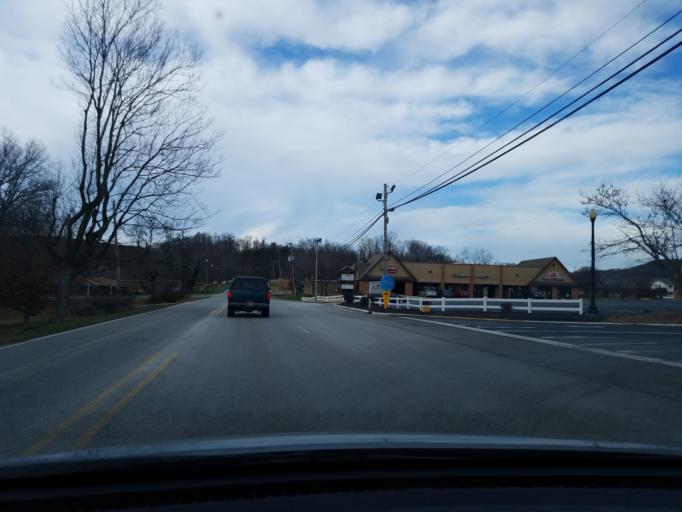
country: US
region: Indiana
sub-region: Floyd County
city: New Albany
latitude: 38.3144
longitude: -85.8517
